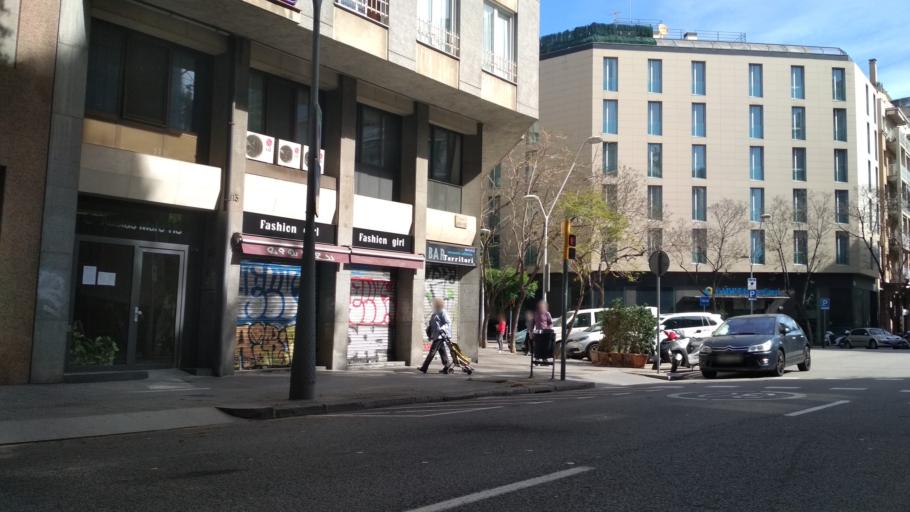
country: ES
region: Catalonia
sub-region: Provincia de Barcelona
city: Ciutat Vella
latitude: 41.3954
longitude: 2.1810
